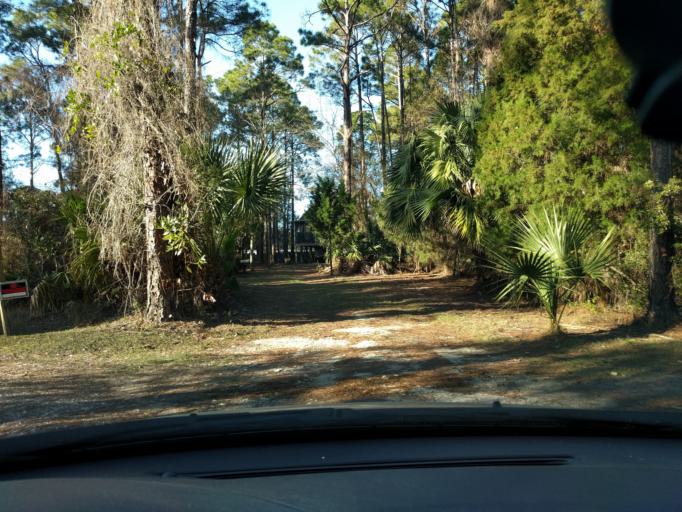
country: US
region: Florida
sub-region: Franklin County
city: Apalachicola
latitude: 29.7155
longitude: -85.0275
